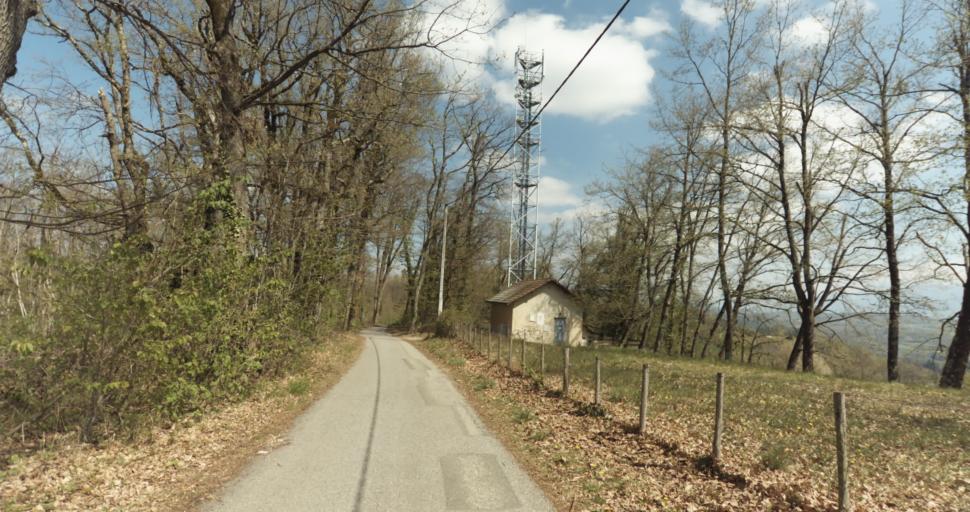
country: FR
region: Rhone-Alpes
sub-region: Departement de l'Isere
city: Saint-Marcellin
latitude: 45.1584
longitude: 5.3050
